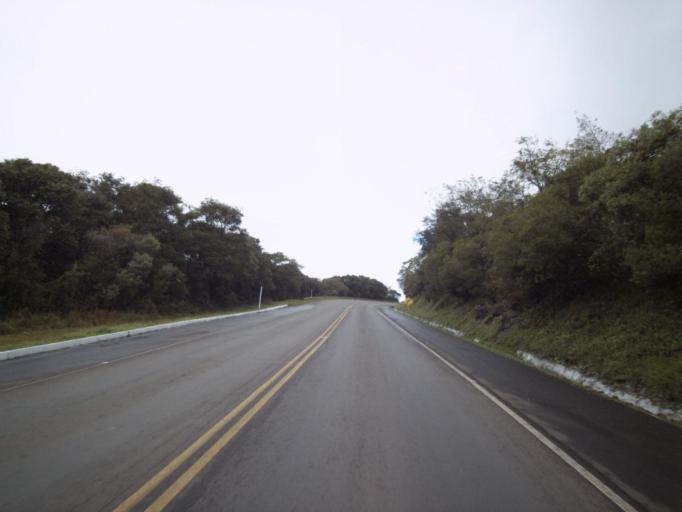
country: BR
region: Santa Catarina
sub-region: Concordia
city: Concordia
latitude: -27.0641
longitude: -51.8931
